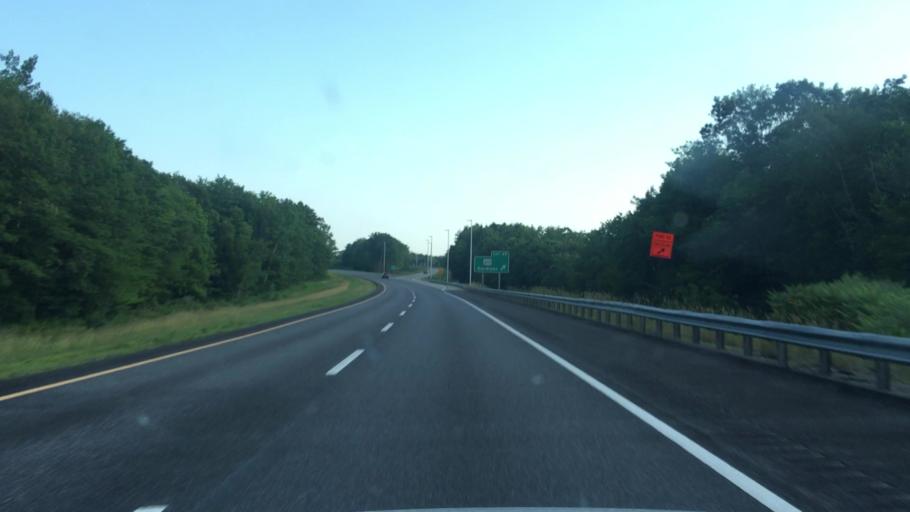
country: US
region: Maine
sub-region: Kennebec County
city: Gardiner
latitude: 44.1842
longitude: -69.8330
